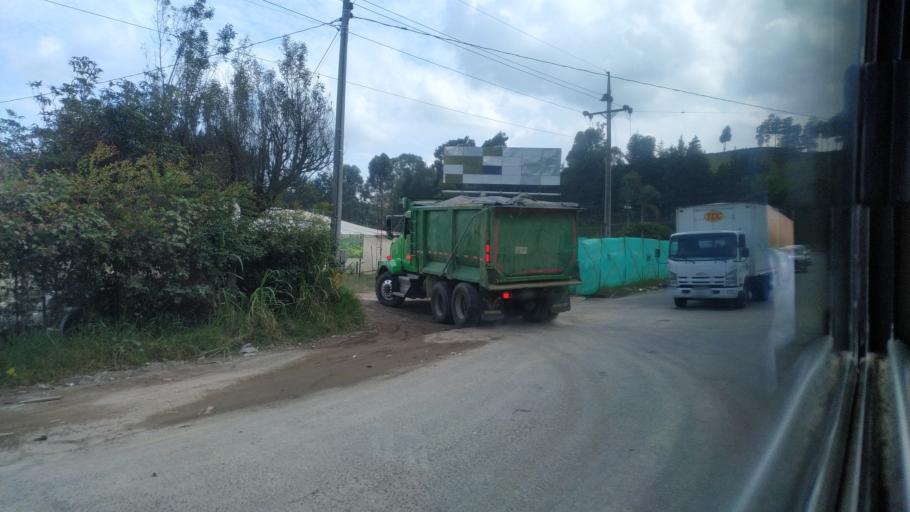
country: CO
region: Antioquia
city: Rionegro
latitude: 6.1725
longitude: -75.3703
